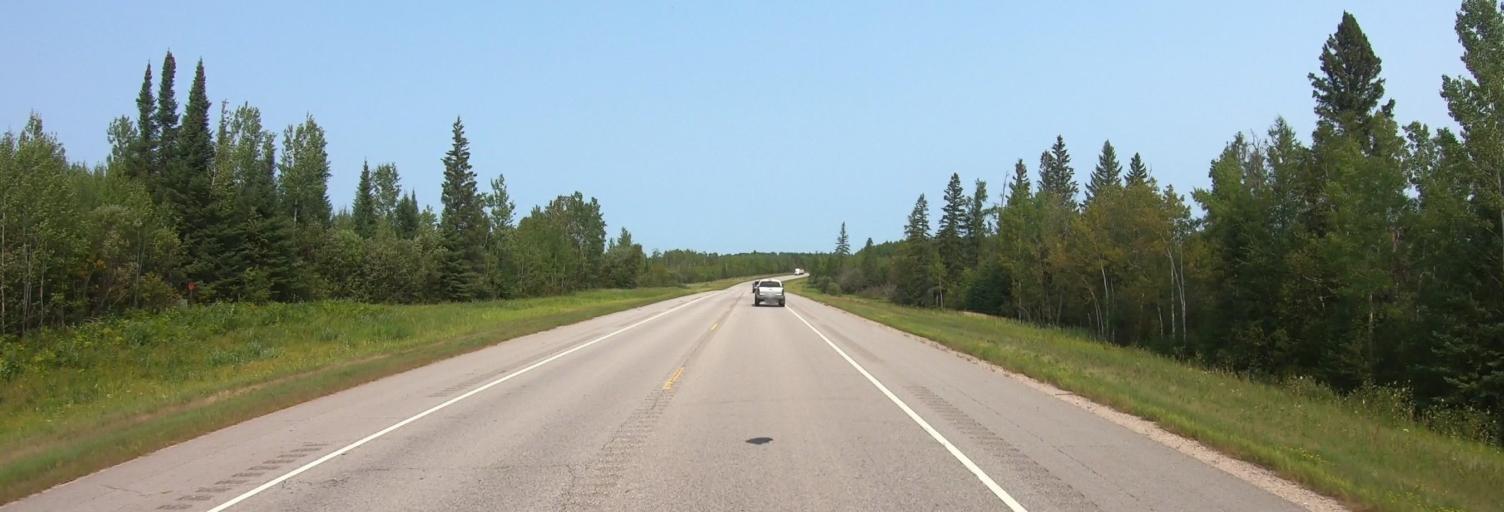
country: CA
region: Ontario
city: Fort Frances
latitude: 48.3278
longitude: -92.9617
